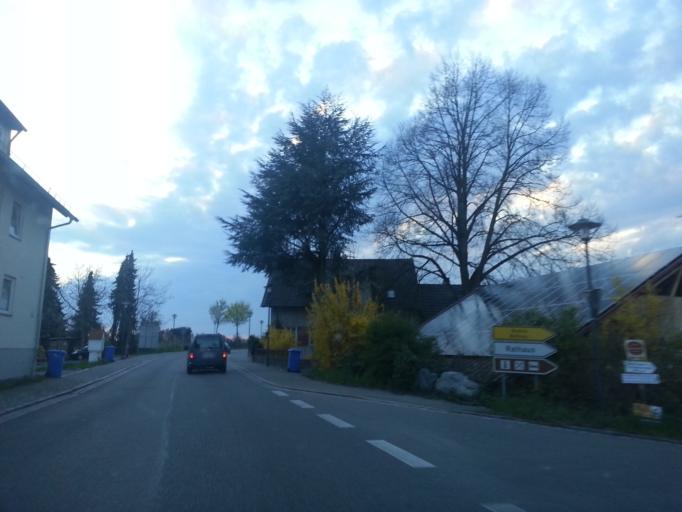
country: DE
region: Bavaria
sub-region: Swabia
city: Bodolz
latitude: 47.5659
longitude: 9.6644
